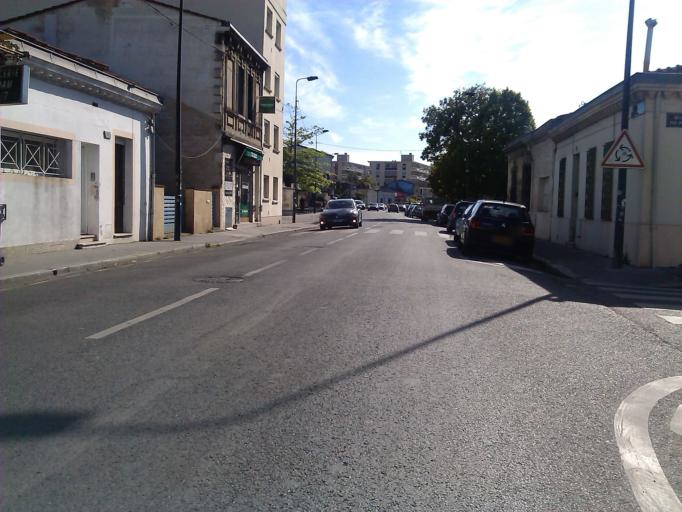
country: FR
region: Aquitaine
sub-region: Departement de la Gironde
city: Talence
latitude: 44.8197
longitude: -0.5975
